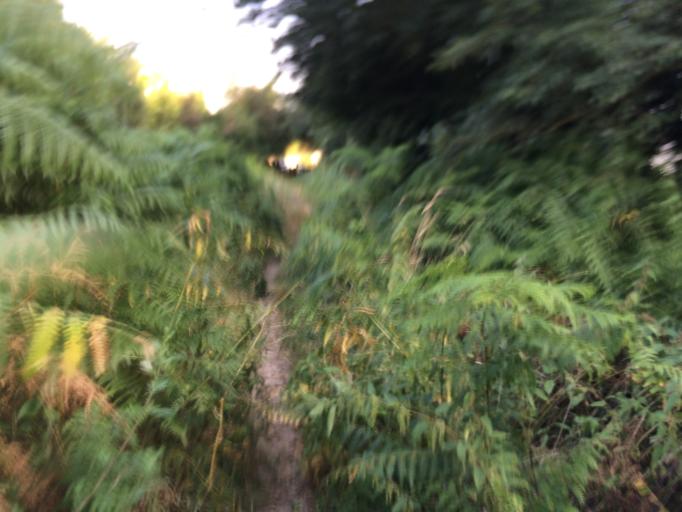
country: FR
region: Ile-de-France
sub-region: Departement de l'Essonne
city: Verrieres-le-Buisson
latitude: 48.7432
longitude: 2.2500
